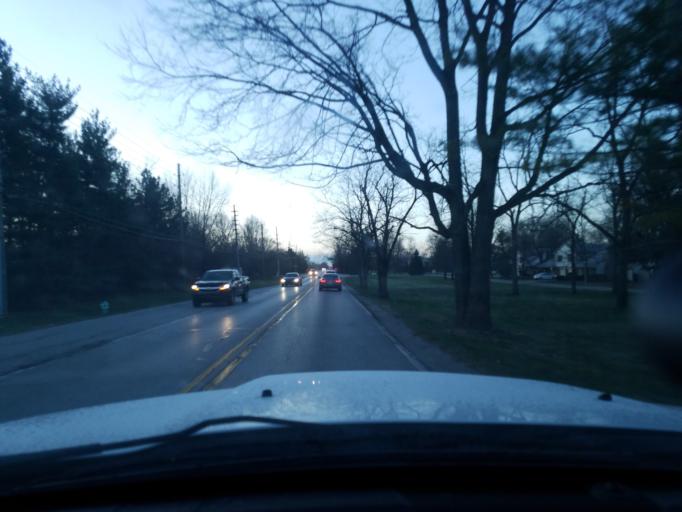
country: US
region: Indiana
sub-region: Marion County
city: Meridian Hills
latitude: 39.9190
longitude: -86.2031
